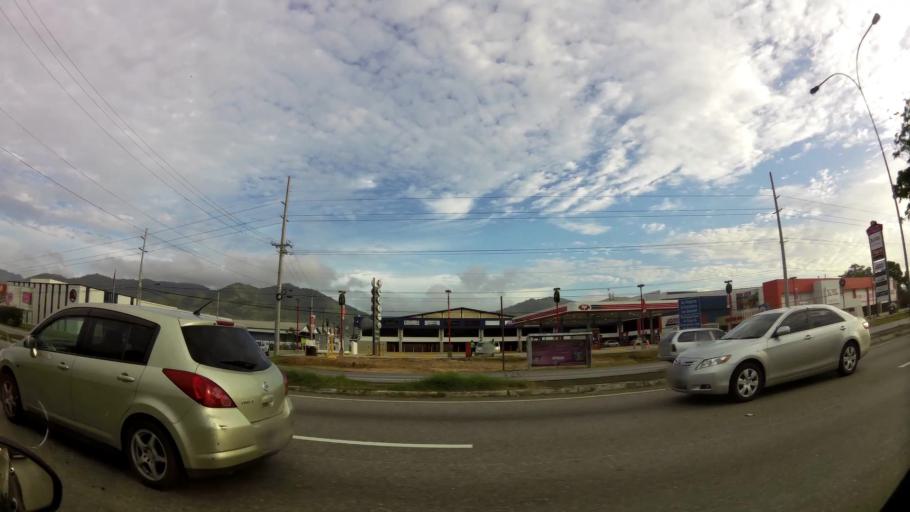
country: TT
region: Tunapuna/Piarco
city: Tunapuna
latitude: 10.6361
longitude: -61.3729
